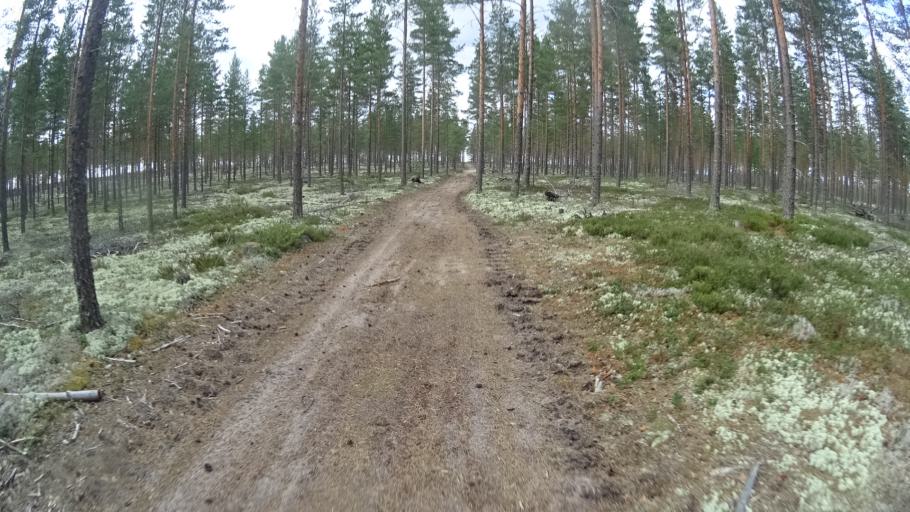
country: FI
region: Satakunta
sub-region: Pohjois-Satakunta
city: Jaemijaervi
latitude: 61.7698
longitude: 22.8035
